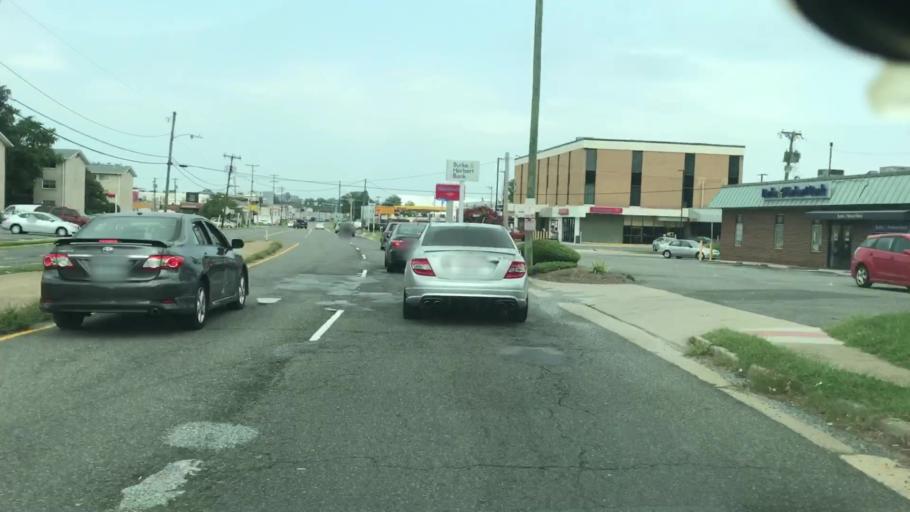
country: US
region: Virginia
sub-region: Fairfax County
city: Baileys Crossroads
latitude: 38.8456
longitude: -77.1238
